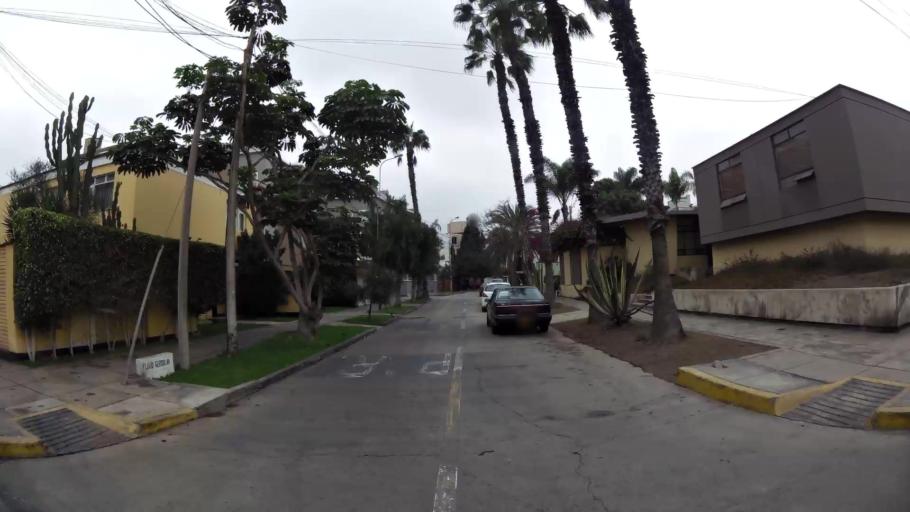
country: PE
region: Lima
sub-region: Lima
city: Surco
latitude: -12.1291
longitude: -77.0131
